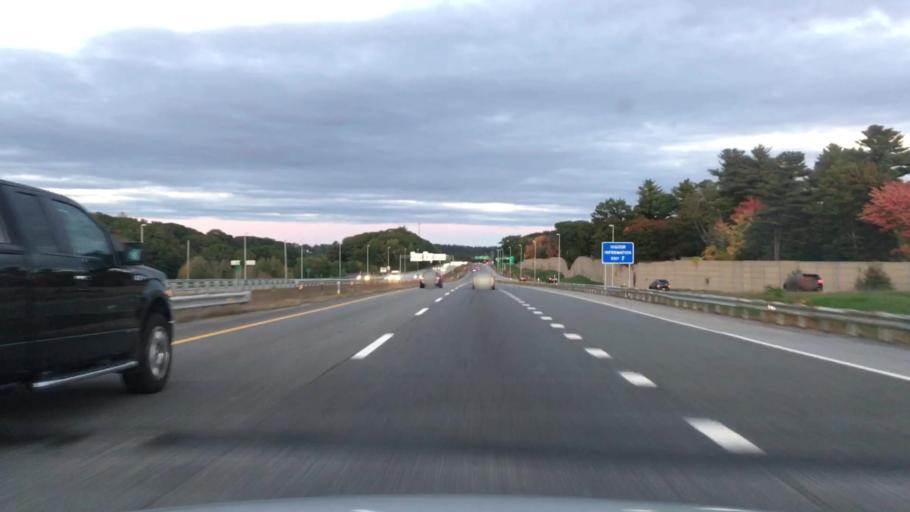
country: US
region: Maine
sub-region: Cumberland County
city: South Portland Gardens
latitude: 43.6313
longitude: -70.3117
